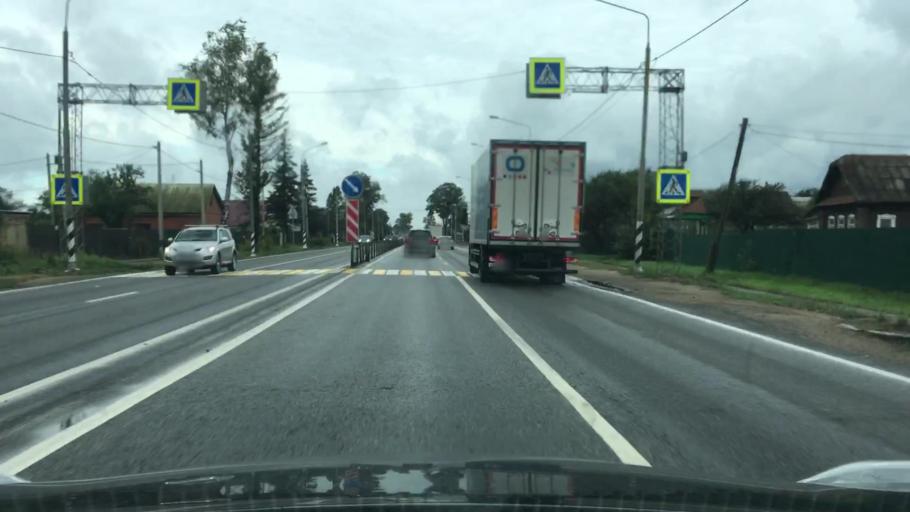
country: RU
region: Moskovskaya
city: Klin
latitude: 56.3841
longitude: 36.6699
